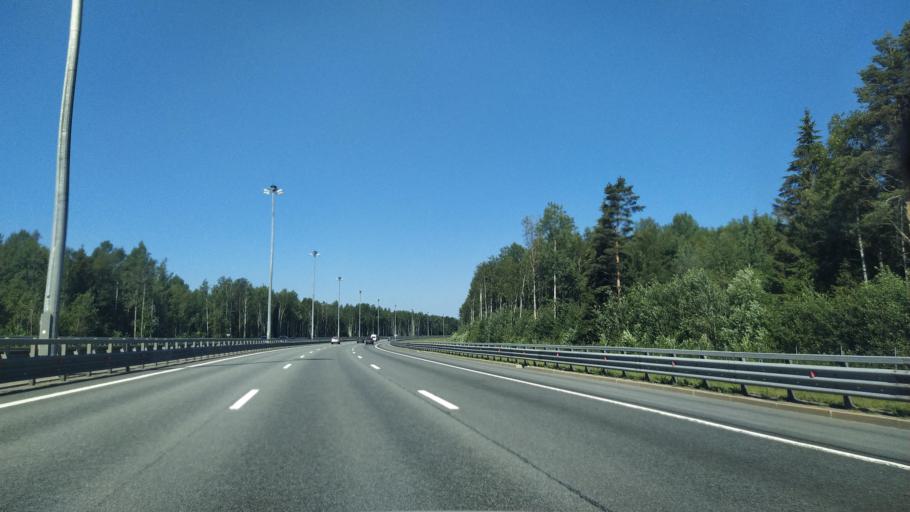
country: RU
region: Leningrad
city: Ol'gino
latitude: 59.8140
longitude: 29.8537
